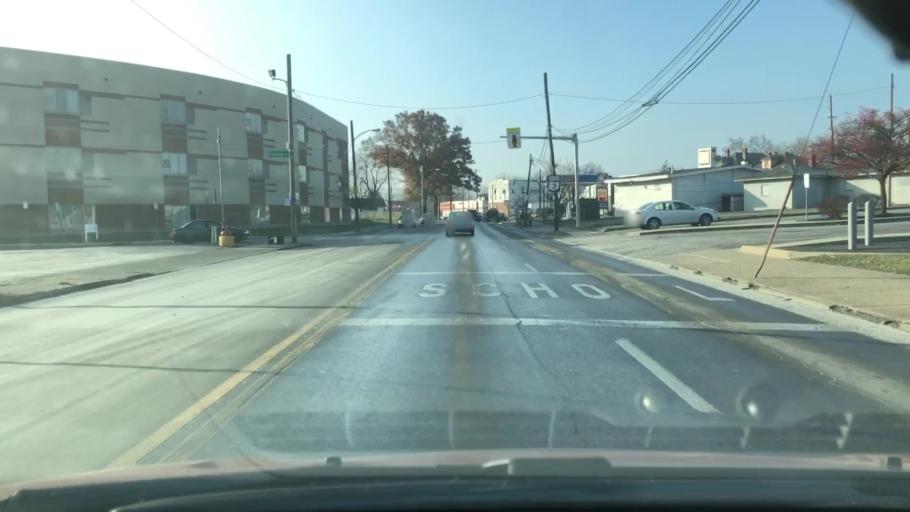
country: US
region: Ohio
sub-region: Franklin County
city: Minerva Park
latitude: 40.0224
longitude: -82.9638
